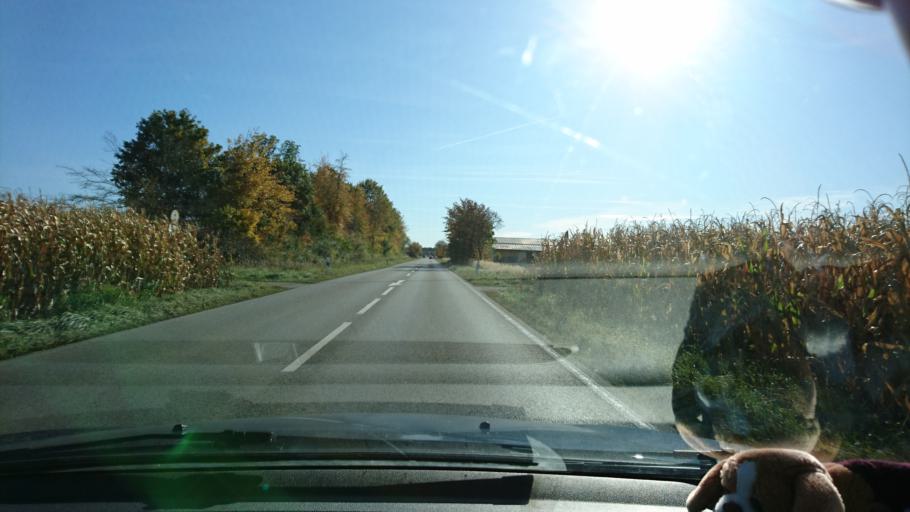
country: DE
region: Bavaria
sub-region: Upper Bavaria
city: Zorneding
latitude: 48.0869
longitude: 11.8175
